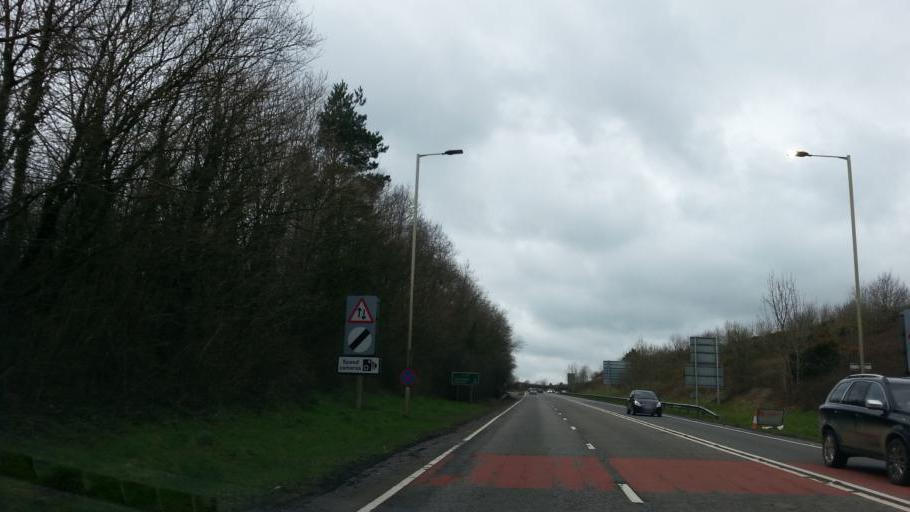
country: GB
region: England
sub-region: Devon
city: South Molton
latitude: 51.0386
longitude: -3.8567
